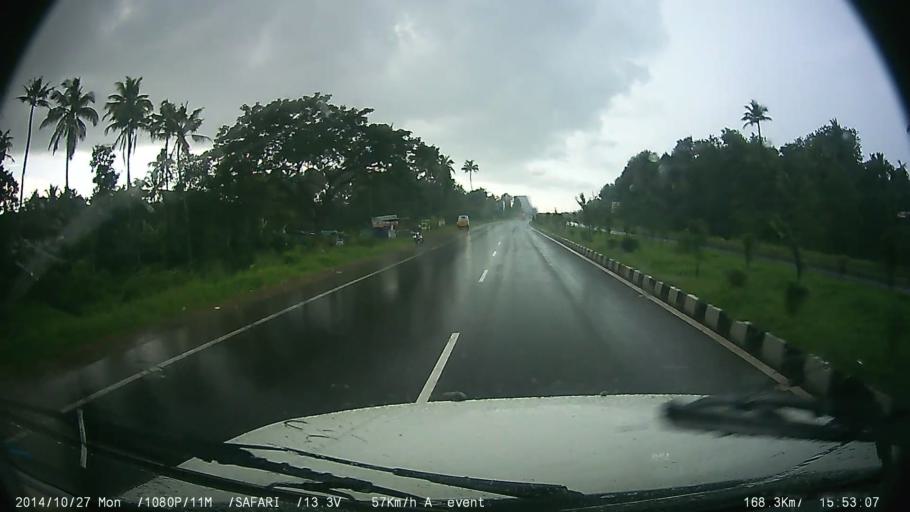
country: IN
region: Kerala
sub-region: Thrissur District
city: Kizhake Chalakudi
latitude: 10.2620
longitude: 76.3564
